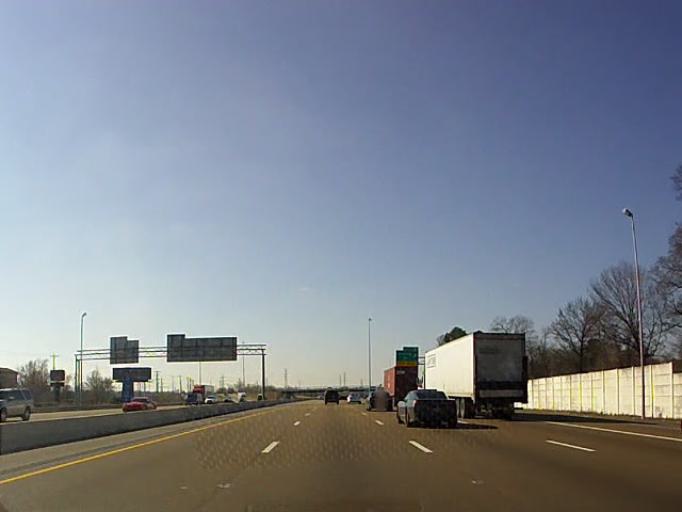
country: US
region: Tennessee
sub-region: Shelby County
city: Germantown
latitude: 35.0796
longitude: -89.9039
